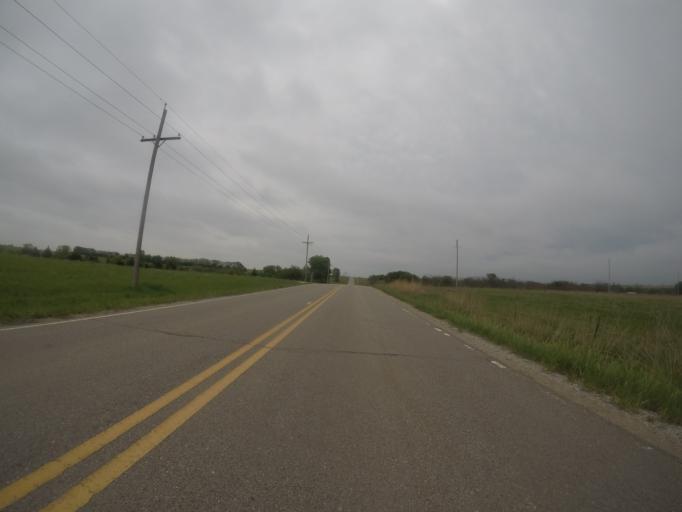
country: US
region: Kansas
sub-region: Pottawatomie County
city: Westmoreland
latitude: 39.5223
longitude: -96.2525
